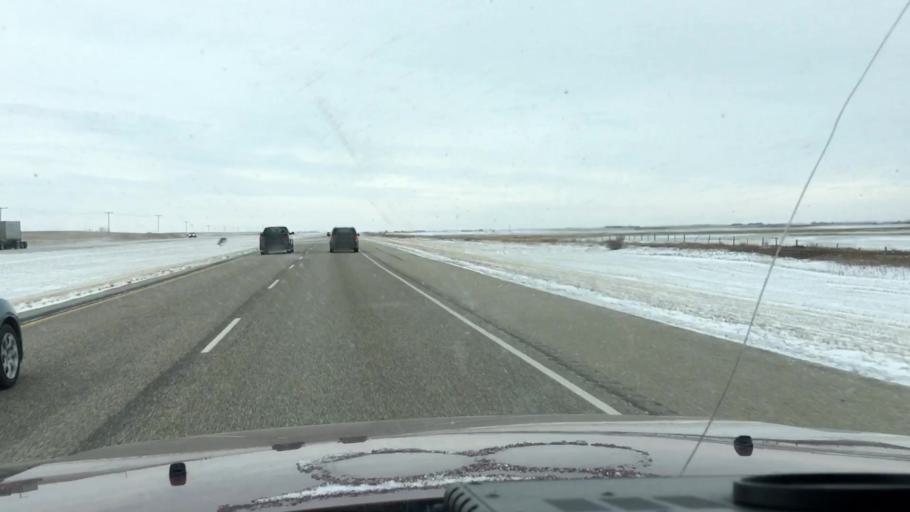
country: CA
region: Saskatchewan
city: Saskatoon
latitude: 51.5990
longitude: -106.3942
